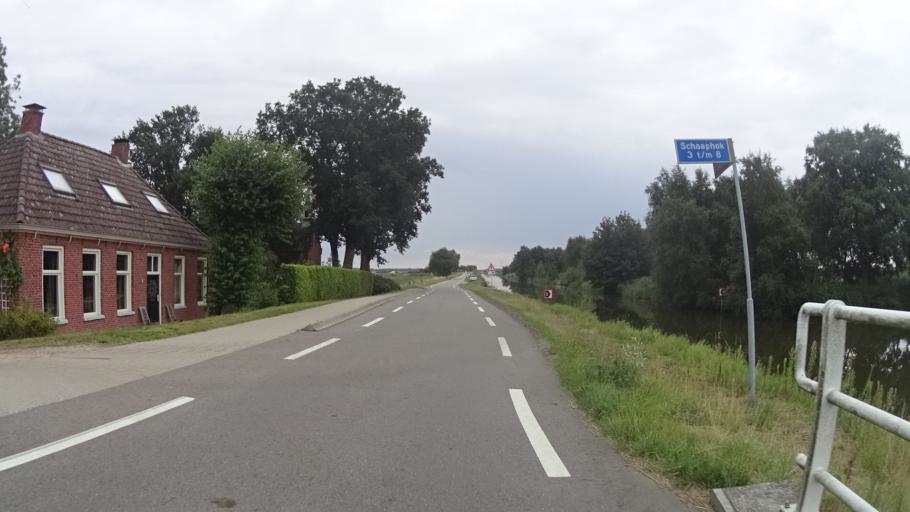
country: NL
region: Groningen
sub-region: Gemeente Slochteren
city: Slochteren
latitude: 53.2348
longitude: 6.7402
